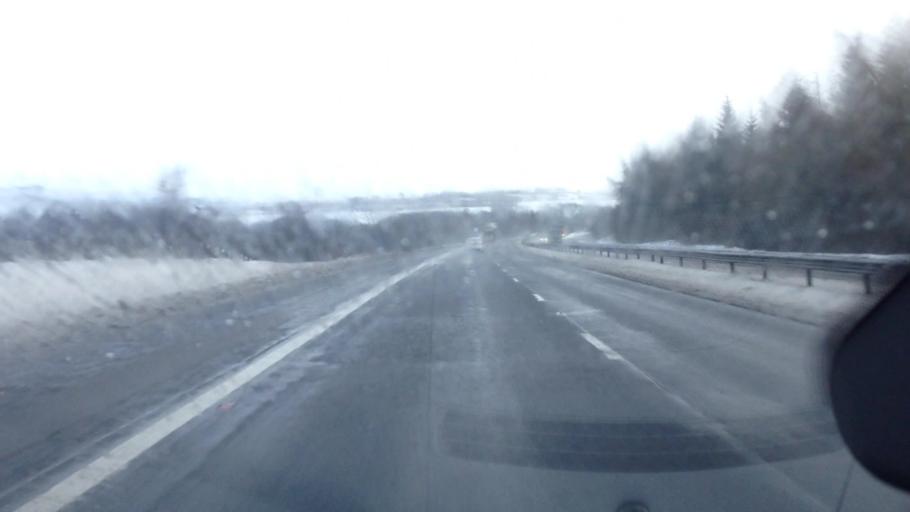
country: GB
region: Scotland
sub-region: South Lanarkshire
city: Blackwood
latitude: 55.6552
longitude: -3.9006
